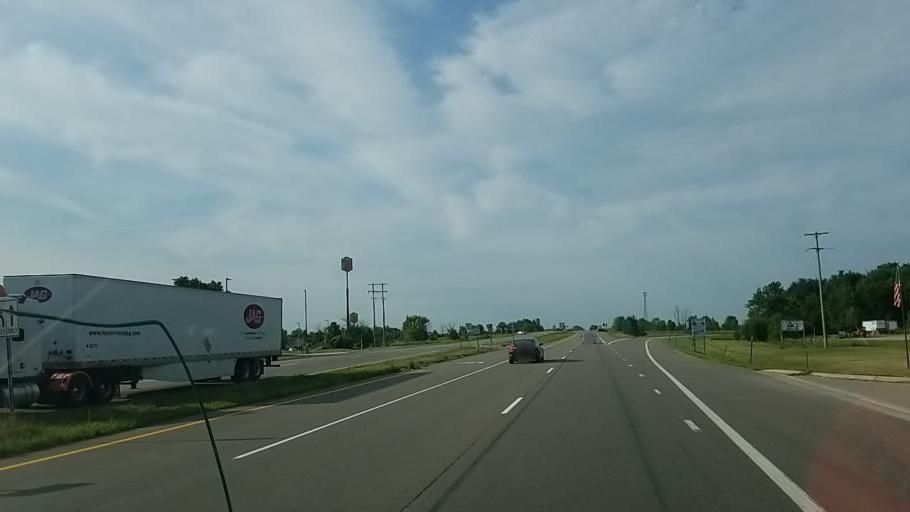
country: US
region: Michigan
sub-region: Ionia County
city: Ionia
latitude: 42.8836
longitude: -85.0751
